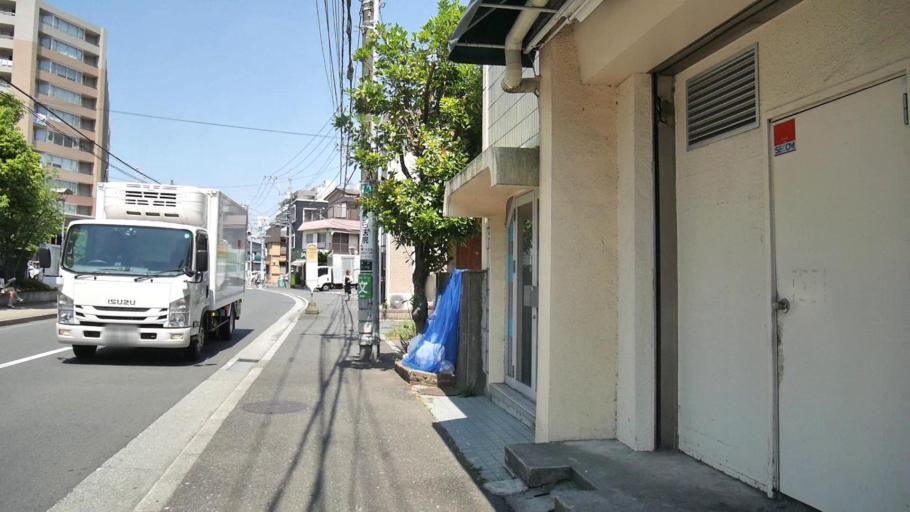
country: JP
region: Kanagawa
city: Fujisawa
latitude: 35.4013
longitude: 139.5194
